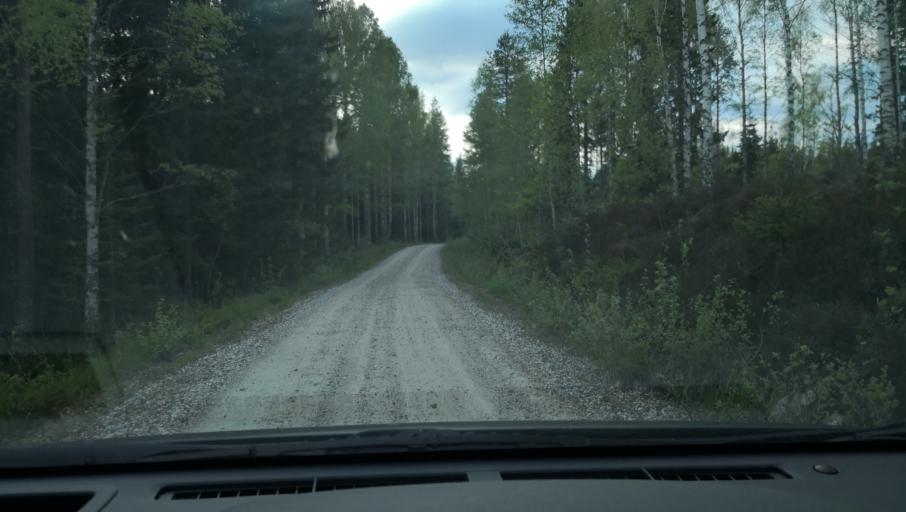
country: SE
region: Vaestmanland
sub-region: Skinnskattebergs Kommun
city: Skinnskatteberg
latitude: 59.7962
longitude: 15.4644
